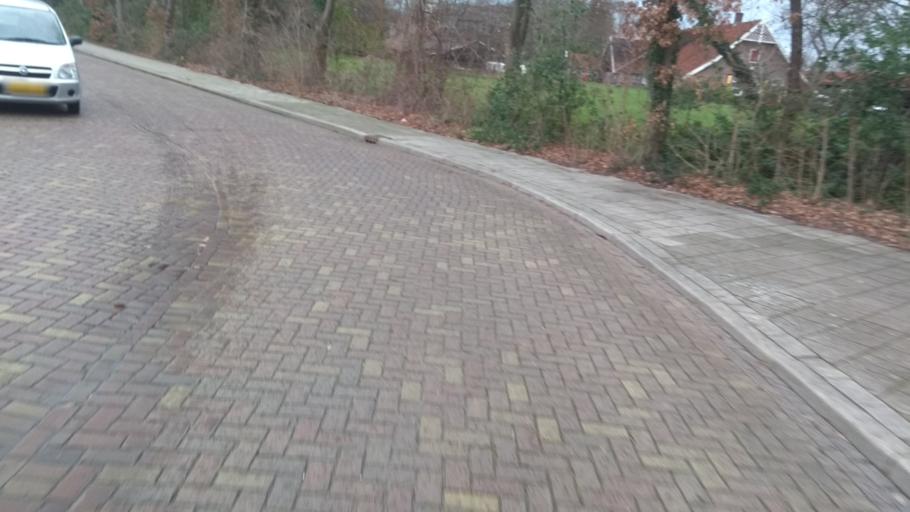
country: NL
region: Overijssel
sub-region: Gemeente Almelo
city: Almelo
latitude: 52.3539
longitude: 6.6812
